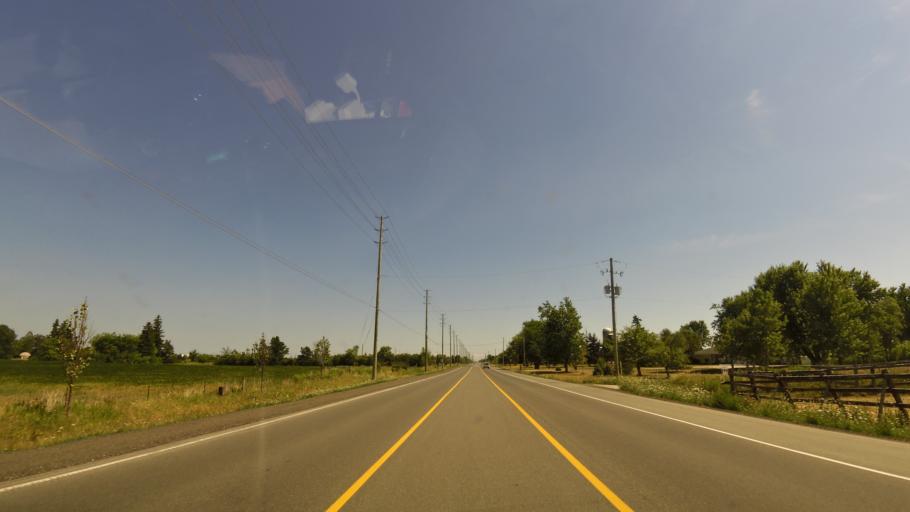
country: CA
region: Ontario
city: Brampton
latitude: 43.6226
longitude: -79.8182
